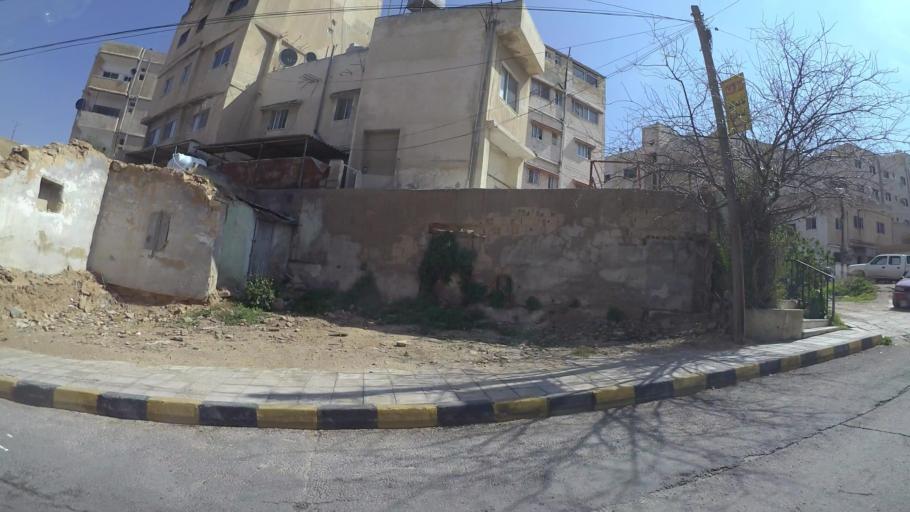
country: JO
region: Amman
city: Amman
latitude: 31.9773
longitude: 35.9774
